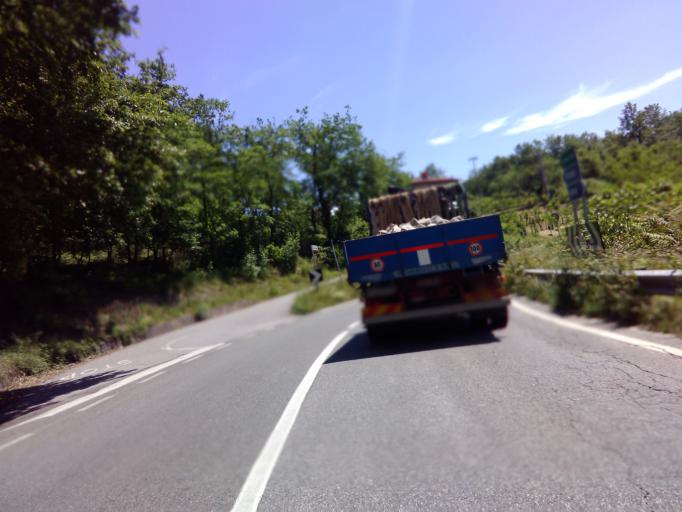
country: IT
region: Tuscany
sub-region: Provincia di Massa-Carrara
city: Barbarasco
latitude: 44.2543
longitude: 9.9579
